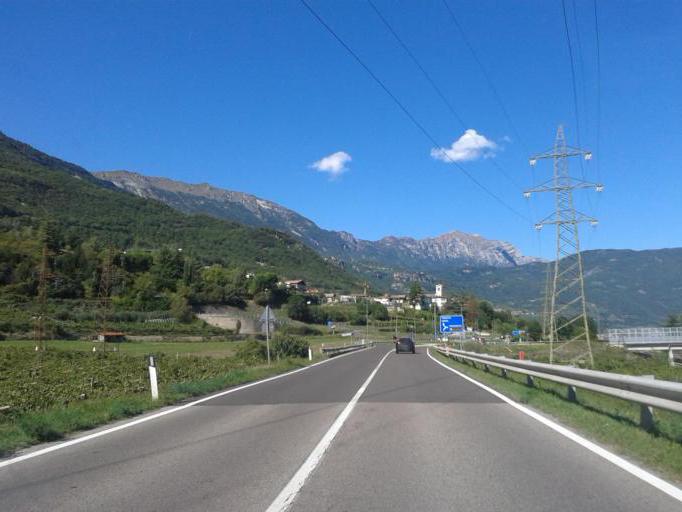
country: IT
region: Trentino-Alto Adige
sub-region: Provincia di Trento
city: Isera
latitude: 45.8794
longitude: 11.0084
